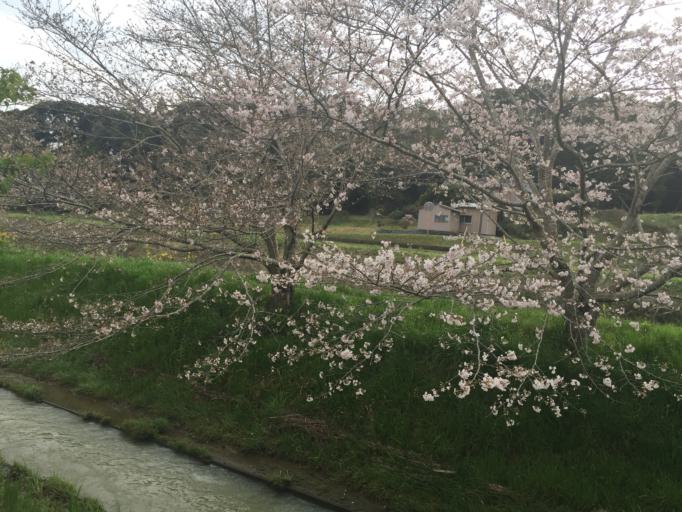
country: JP
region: Shizuoka
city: Mori
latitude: 34.8014
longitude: 137.9750
